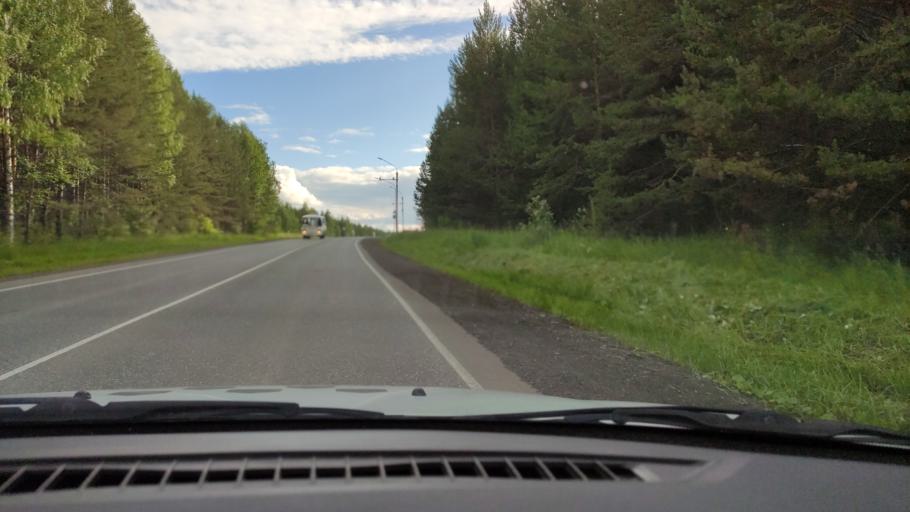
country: RU
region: Perm
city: Kungur
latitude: 57.4118
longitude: 56.9100
